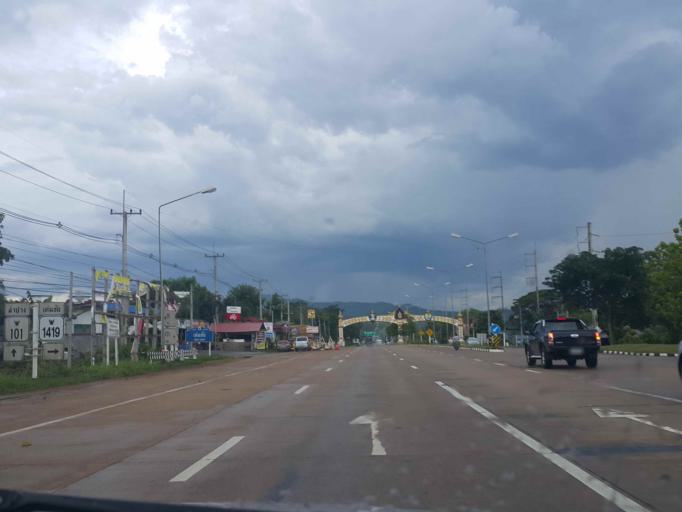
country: TH
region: Phrae
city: Den Chai
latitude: 17.9731
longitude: 100.0772
